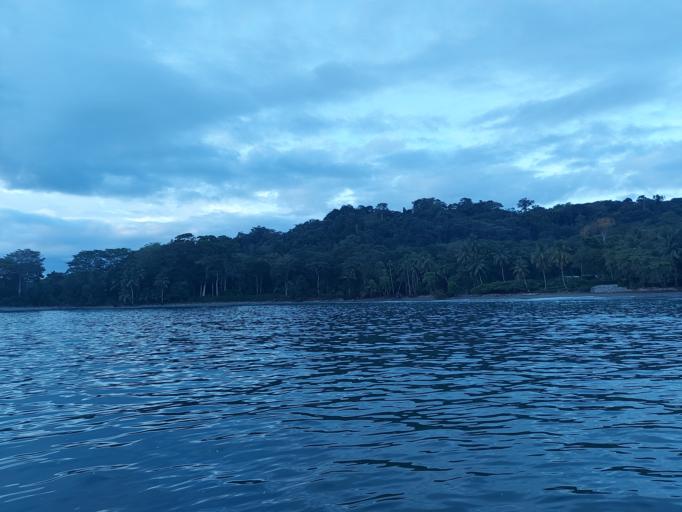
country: CR
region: Puntarenas
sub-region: Canton de Golfito
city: Golfito
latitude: 8.3996
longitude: -83.2801
